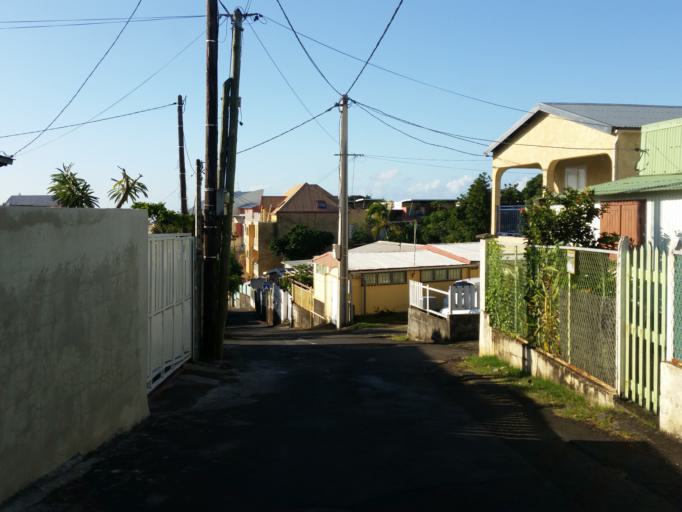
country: RE
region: Reunion
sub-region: Reunion
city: Saint-Denis
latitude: -20.8980
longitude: 55.4695
